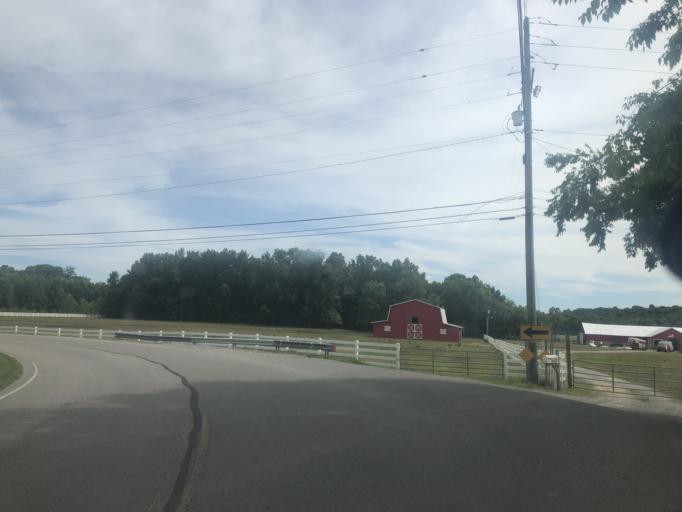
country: US
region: Tennessee
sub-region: Davidson County
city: Lakewood
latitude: 36.1997
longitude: -86.6649
